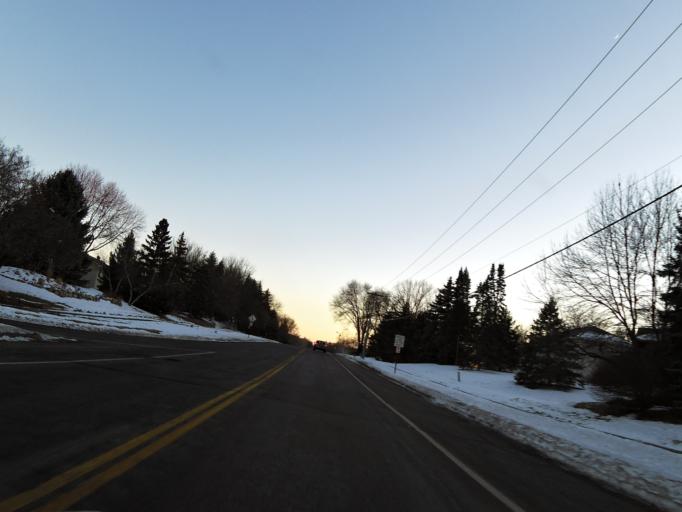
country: US
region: Minnesota
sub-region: Scott County
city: Savage
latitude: 44.8271
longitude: -93.3585
